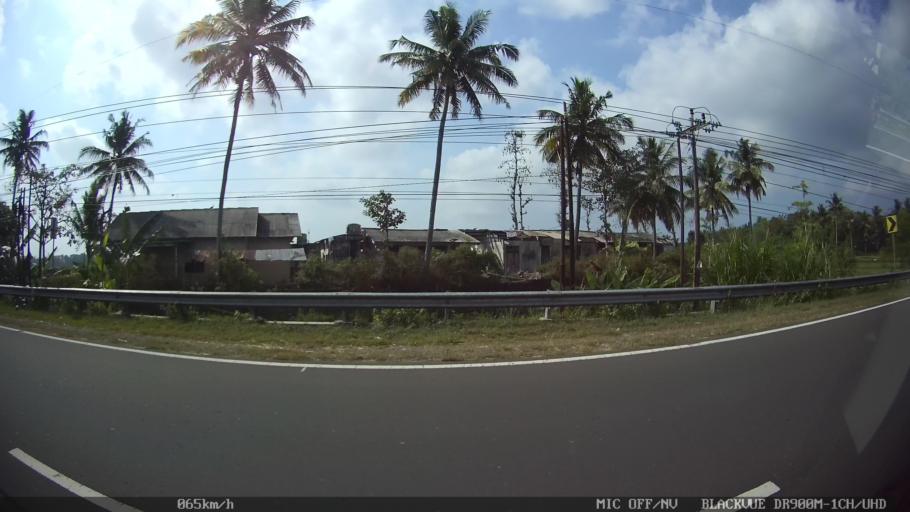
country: ID
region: Daerah Istimewa Yogyakarta
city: Srandakan
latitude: -7.8750
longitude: 110.2076
